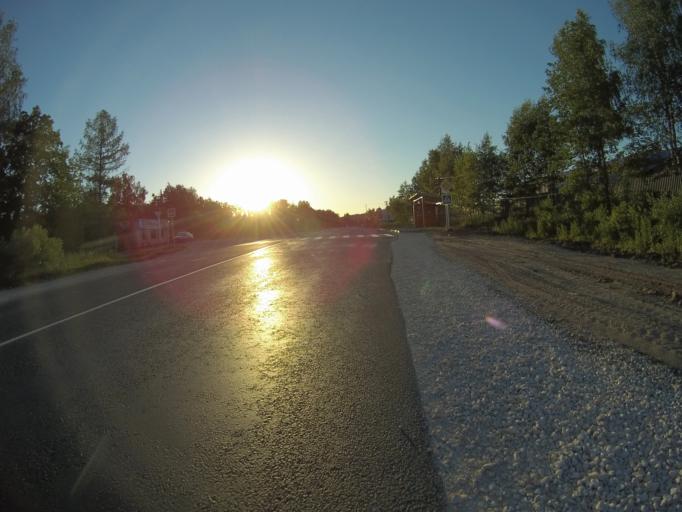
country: RU
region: Vladimir
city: Kommunar
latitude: 56.0493
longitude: 40.5325
